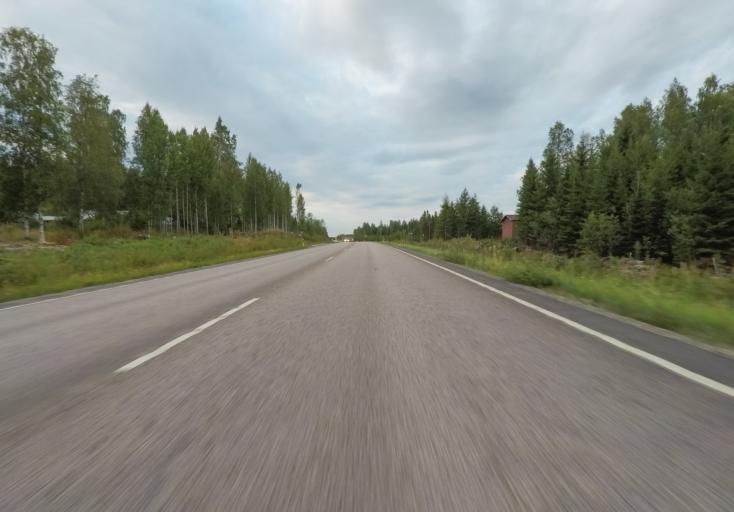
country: FI
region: Central Finland
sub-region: Joutsa
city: Leivonmaeki
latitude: 61.8516
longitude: 26.1015
